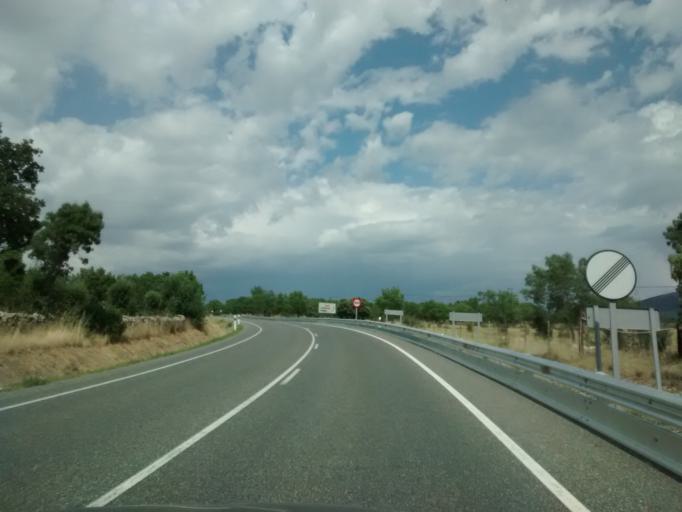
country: ES
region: Castille and Leon
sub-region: Provincia de Segovia
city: Gallegos
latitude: 41.0787
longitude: -3.8013
